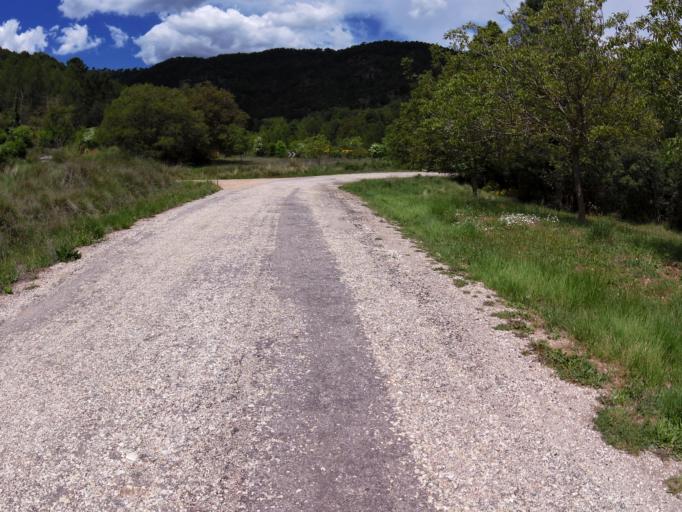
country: ES
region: Castille-La Mancha
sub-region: Provincia de Albacete
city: Paterna del Madera
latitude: 38.5784
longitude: -2.3417
